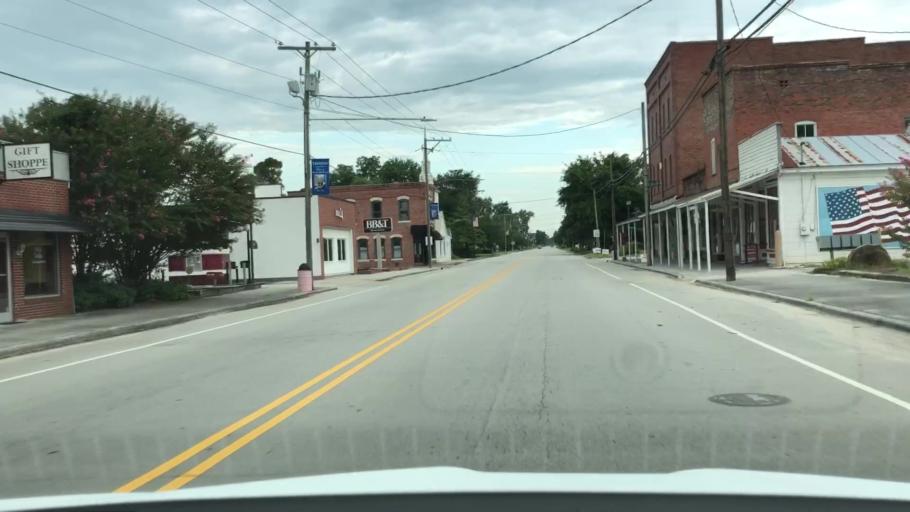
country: US
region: North Carolina
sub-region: Jones County
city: Trenton
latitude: 35.0639
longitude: -77.3543
